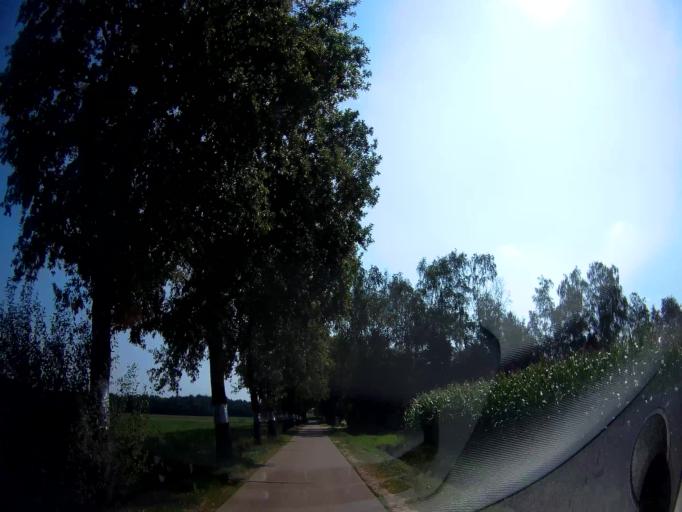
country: BE
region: Flanders
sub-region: Provincie Antwerpen
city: Oud-Turnhout
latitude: 51.2770
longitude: 5.0225
